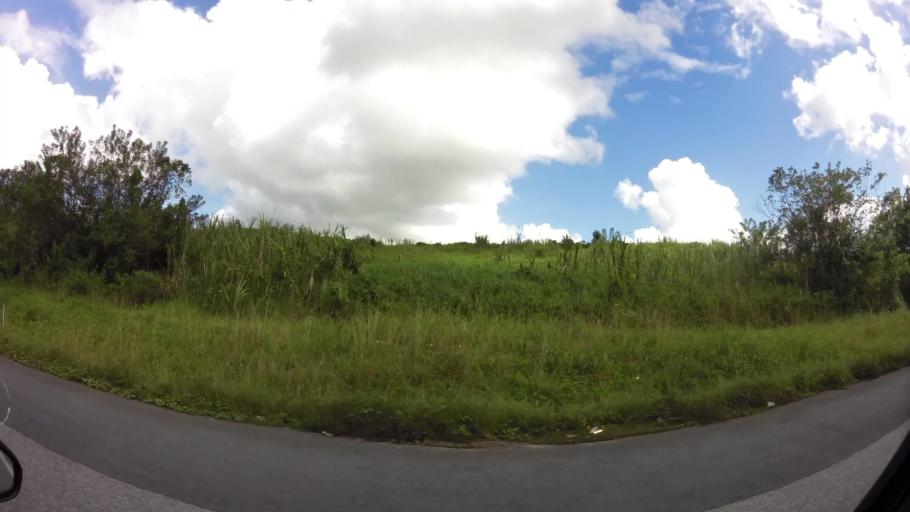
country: TT
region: Penal/Debe
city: Debe
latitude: 10.2400
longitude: -61.4378
